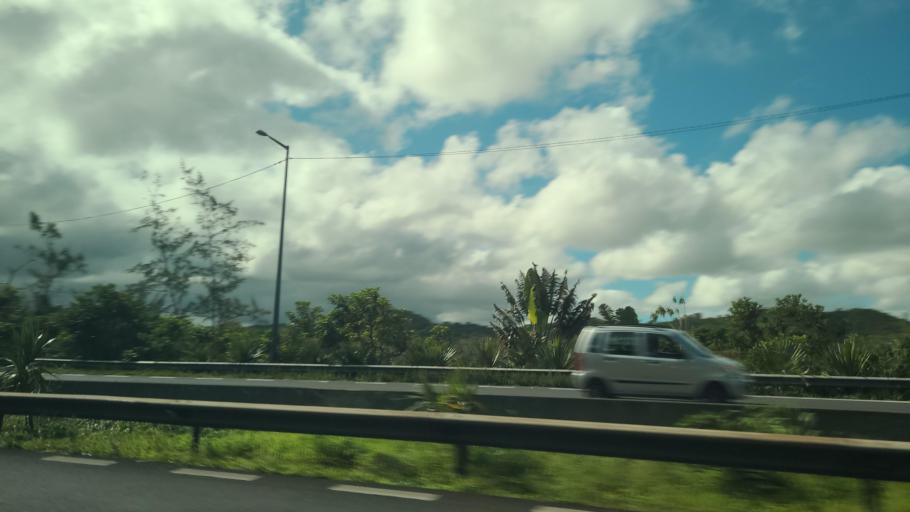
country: MU
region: Plaines Wilhems
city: Midlands
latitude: -20.3310
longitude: 57.5561
